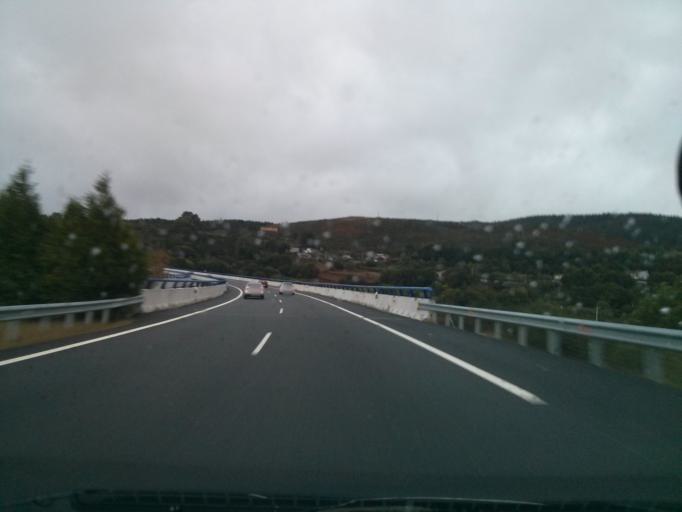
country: ES
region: Galicia
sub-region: Provincia de Pontevedra
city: Covelo
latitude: 42.1971
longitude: -8.3044
